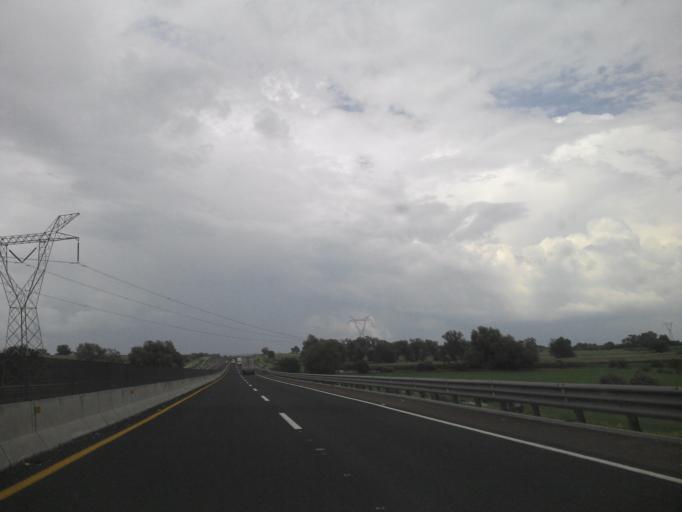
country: MX
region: Hidalgo
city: San Marcos
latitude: 20.0798
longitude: -99.3424
